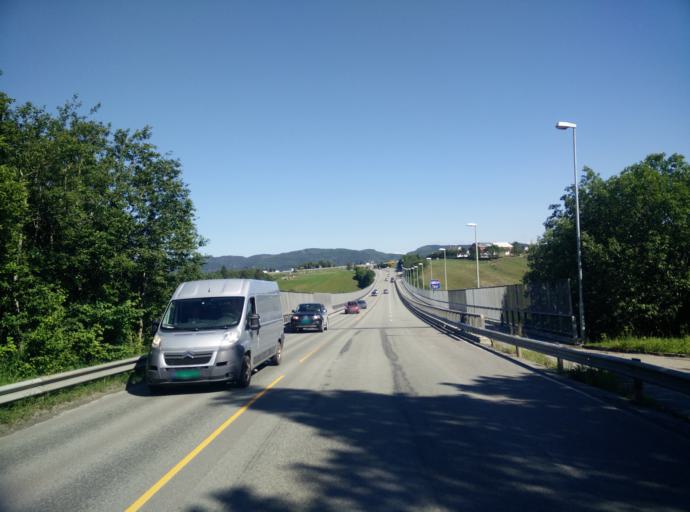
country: NO
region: Sor-Trondelag
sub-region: Trondheim
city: Trondheim
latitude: 63.3709
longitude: 10.3643
